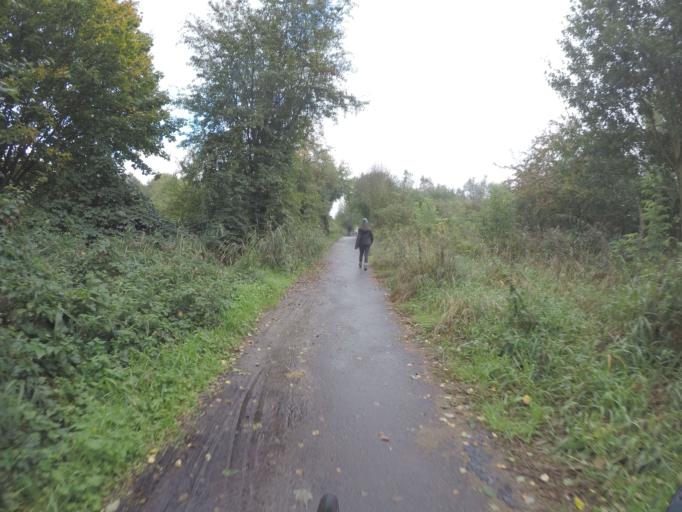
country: DE
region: Berlin
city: Lubars
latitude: 52.6239
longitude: 13.3689
